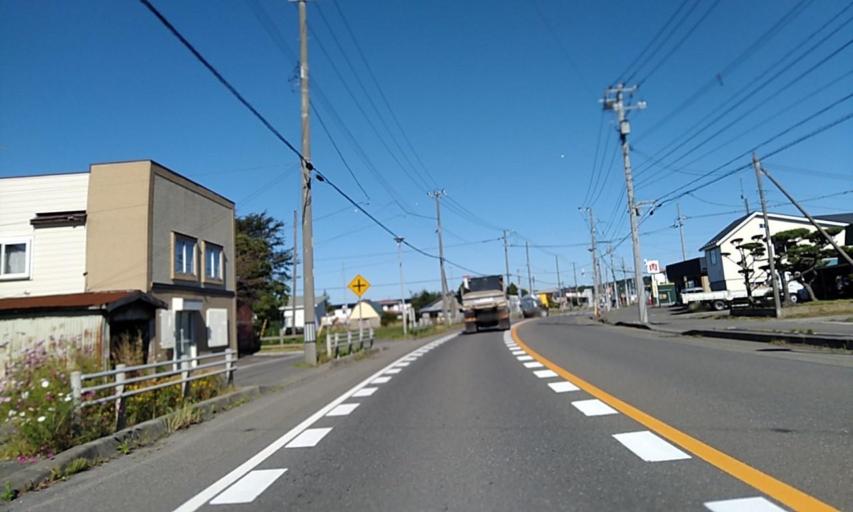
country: JP
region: Hokkaido
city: Shizunai-furukawacho
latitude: 42.5086
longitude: 142.0369
